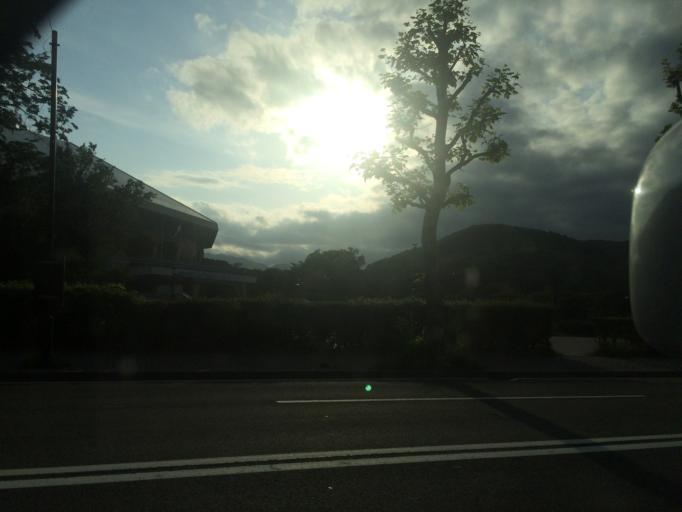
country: JP
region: Hokkaido
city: Sapporo
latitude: 43.0000
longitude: 141.3487
